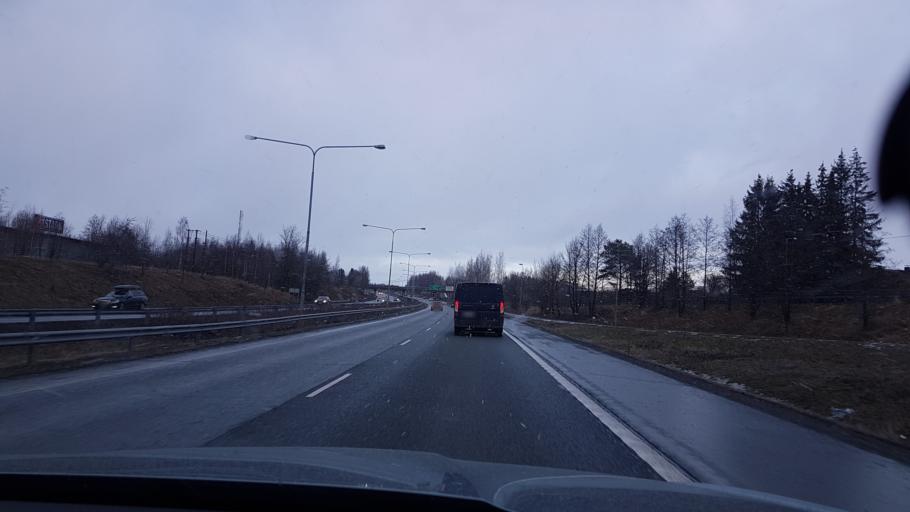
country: FI
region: Pirkanmaa
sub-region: Tampere
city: Tampere
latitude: 61.4792
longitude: 23.8721
